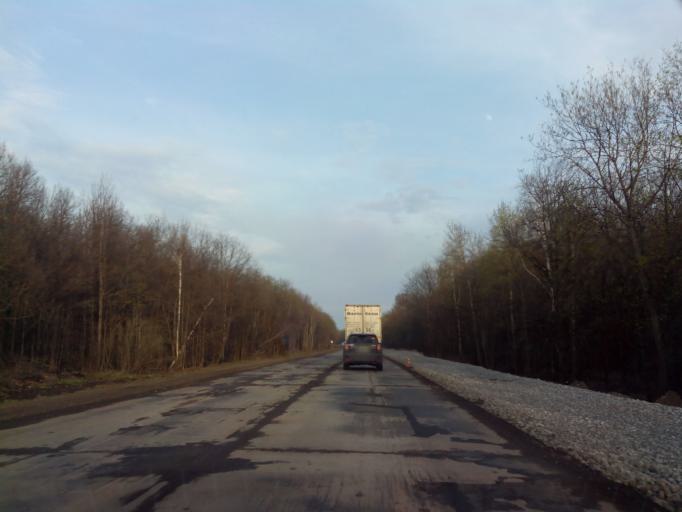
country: RU
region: Rjazan
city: Zarechnyy
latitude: 53.7544
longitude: 39.7921
